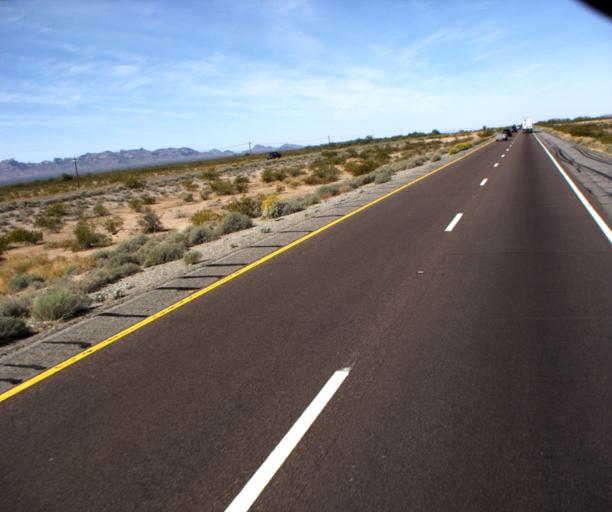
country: US
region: Arizona
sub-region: La Paz County
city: Salome
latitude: 33.5566
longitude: -113.2692
